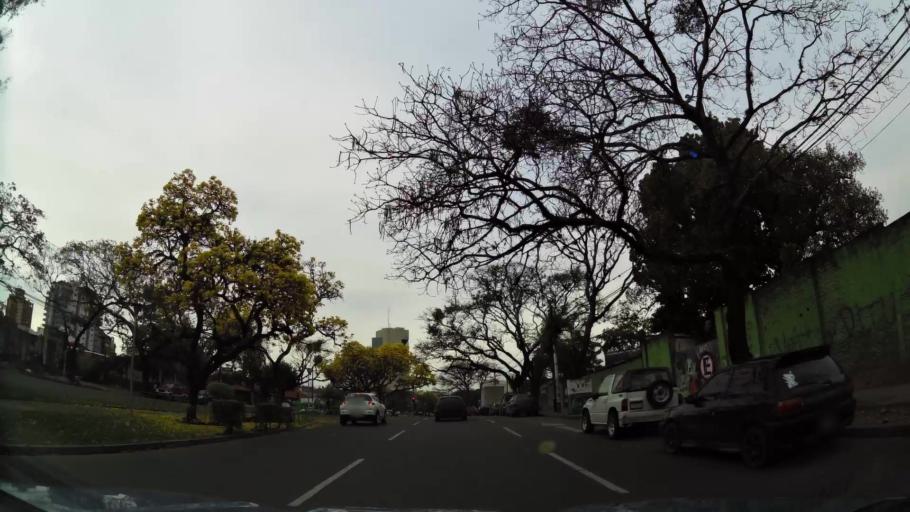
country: BO
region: Santa Cruz
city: Santa Cruz de la Sierra
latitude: -17.7758
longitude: -63.1853
